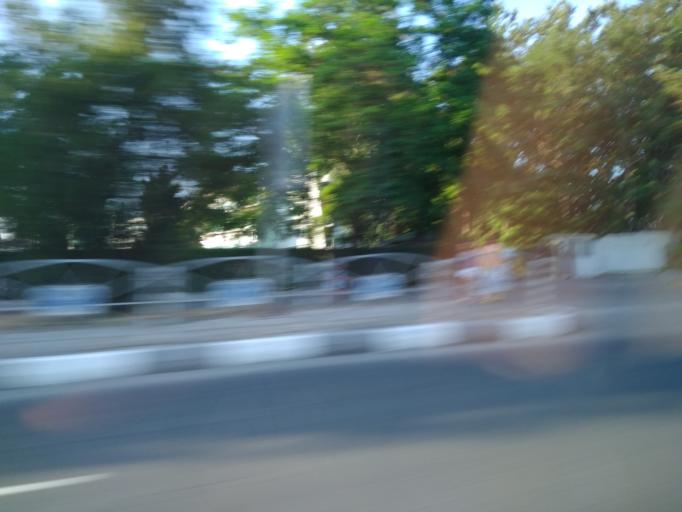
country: BG
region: Burgas
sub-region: Obshtina Nesebur
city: Nesebar
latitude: 42.6655
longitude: 27.7083
